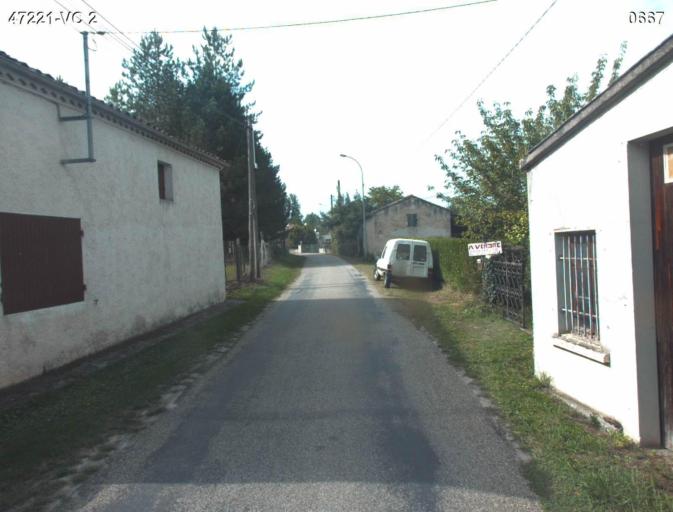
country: FR
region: Aquitaine
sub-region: Departement du Lot-et-Garonne
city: Mezin
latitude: 44.1064
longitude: 0.2335
